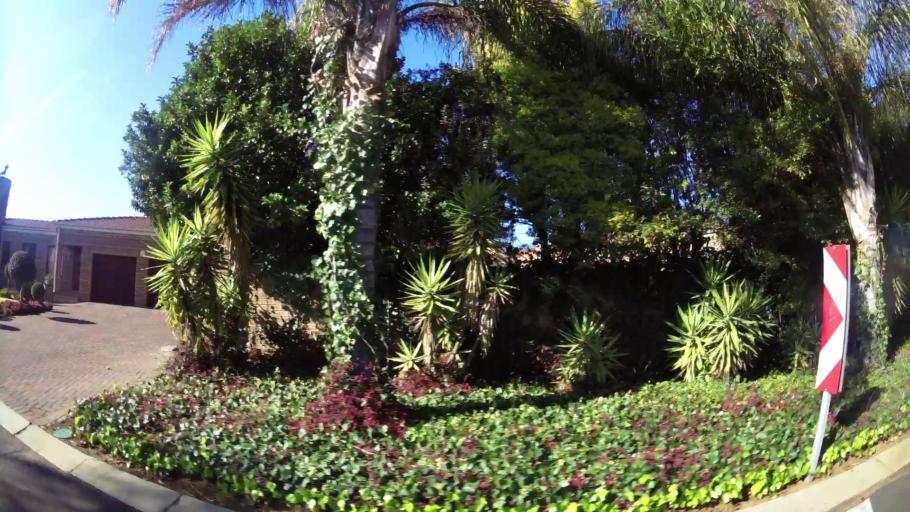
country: ZA
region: Mpumalanga
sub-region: Nkangala District Municipality
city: Witbank
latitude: -25.8906
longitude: 29.2486
